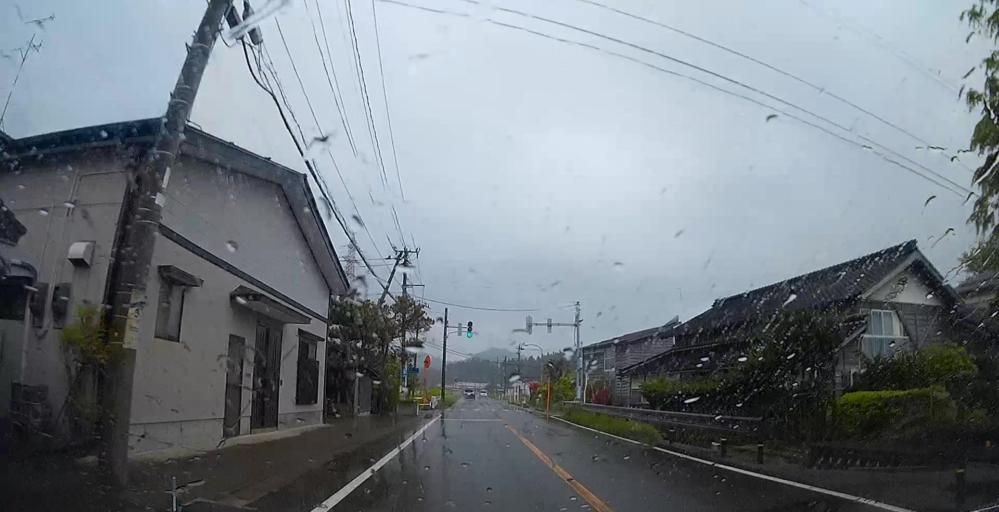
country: JP
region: Niigata
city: Kashiwazaki
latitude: 37.4458
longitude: 138.6479
